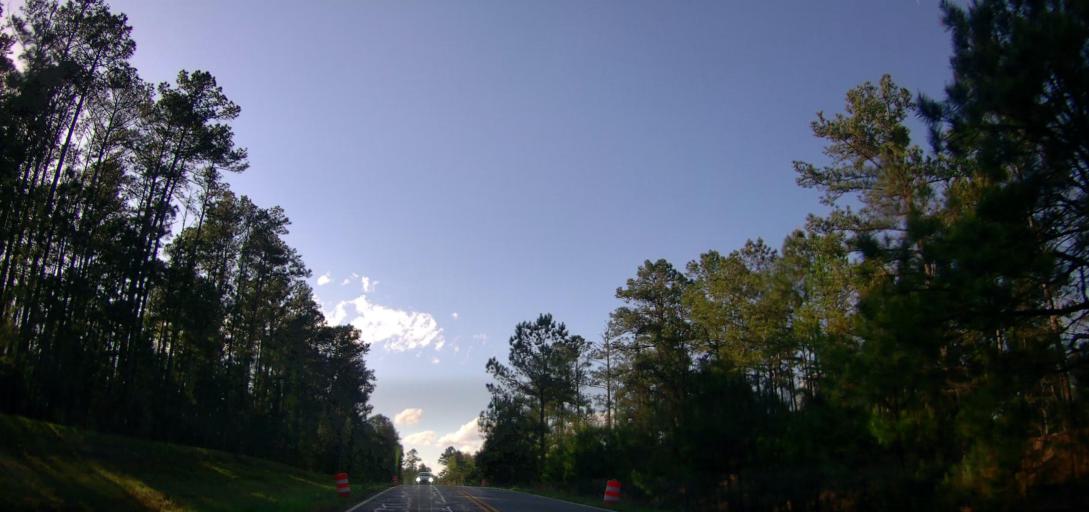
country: US
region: Georgia
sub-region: Baldwin County
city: Milledgeville
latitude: 33.1226
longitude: -83.2938
